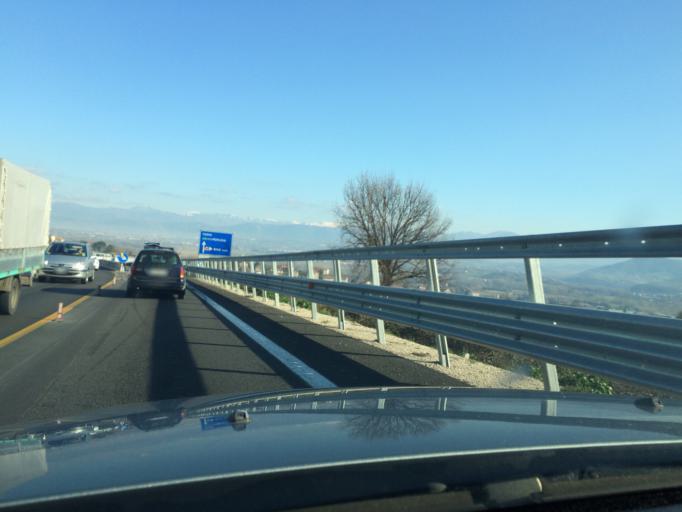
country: IT
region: Umbria
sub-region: Provincia di Terni
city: Narni Scalo
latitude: 42.5396
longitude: 12.5042
